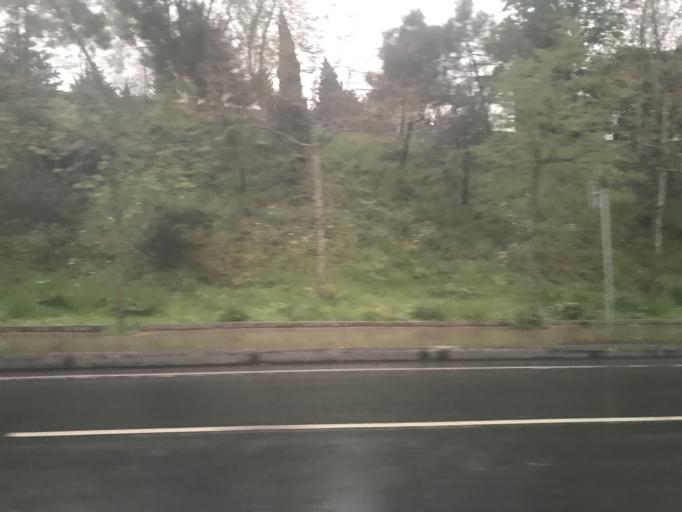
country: TR
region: Istanbul
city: Istanbul
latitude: 41.0512
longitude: 28.9470
